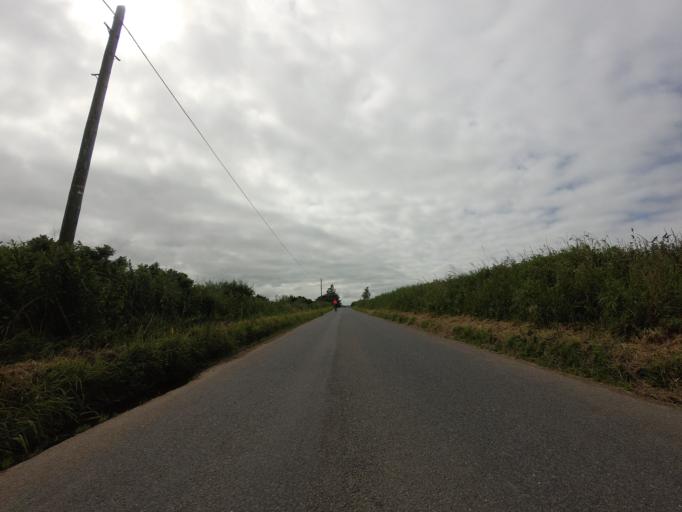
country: GB
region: Scotland
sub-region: Aberdeenshire
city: Turriff
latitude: 57.5438
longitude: -2.2529
